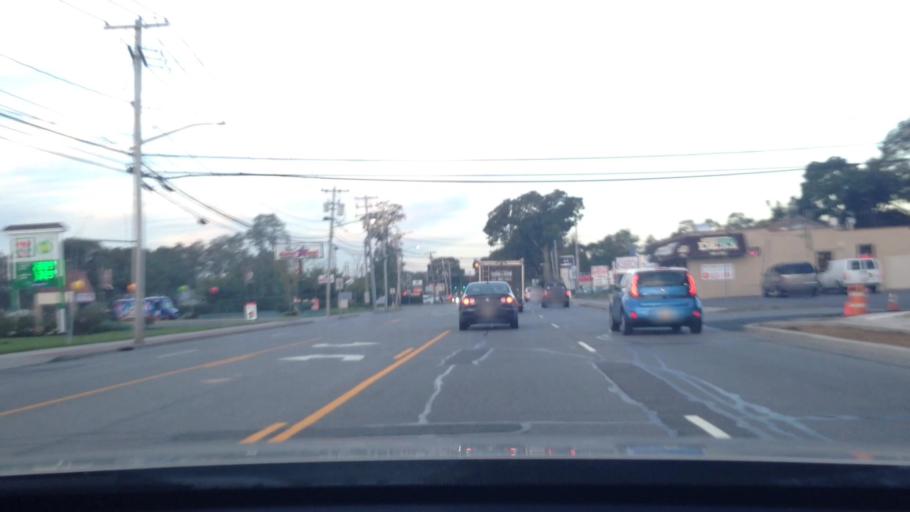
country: US
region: New York
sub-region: Suffolk County
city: Centereach
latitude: 40.8601
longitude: -73.0729
